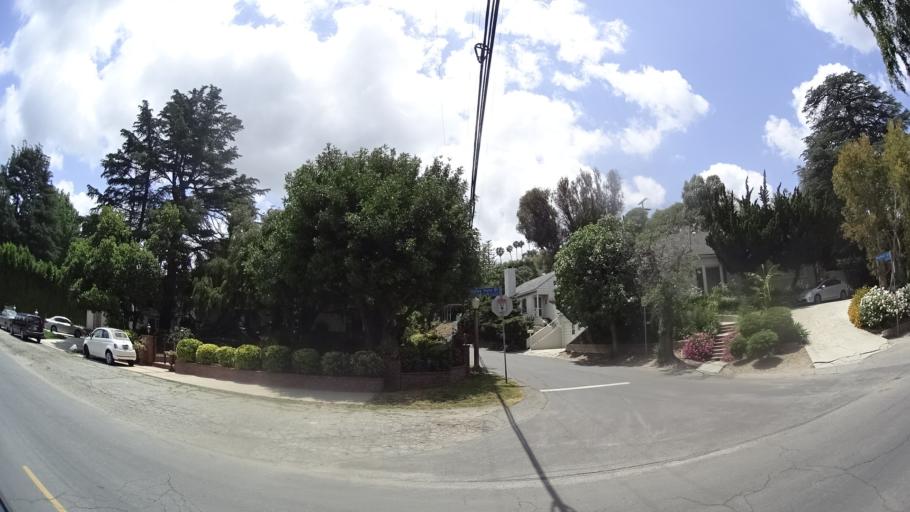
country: US
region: California
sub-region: Los Angeles County
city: Sherman Oaks
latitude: 34.1447
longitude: -118.4300
